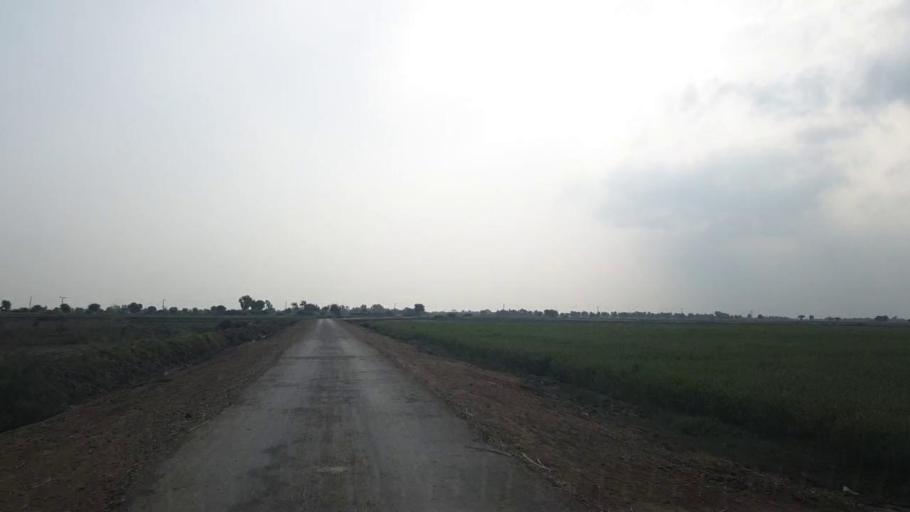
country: PK
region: Sindh
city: Badin
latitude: 24.6466
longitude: 68.6979
